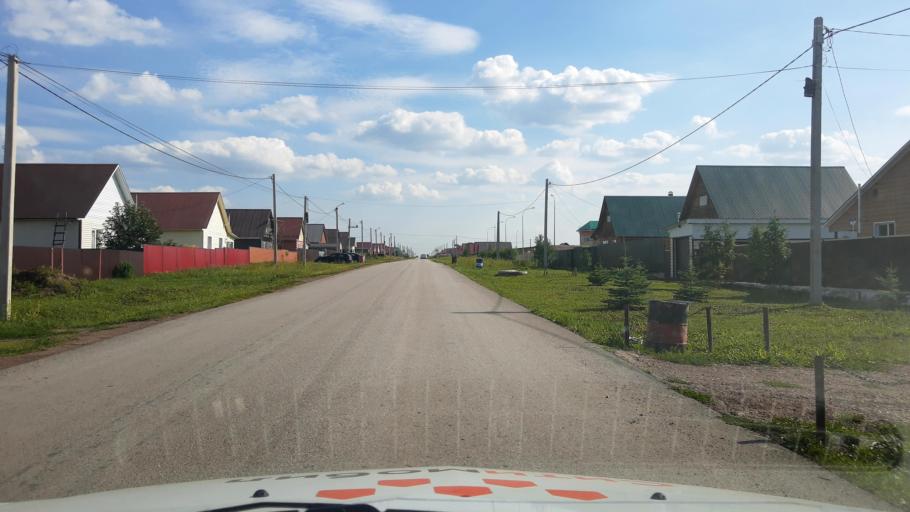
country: RU
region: Bashkortostan
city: Kabakovo
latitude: 54.6545
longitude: 56.2141
